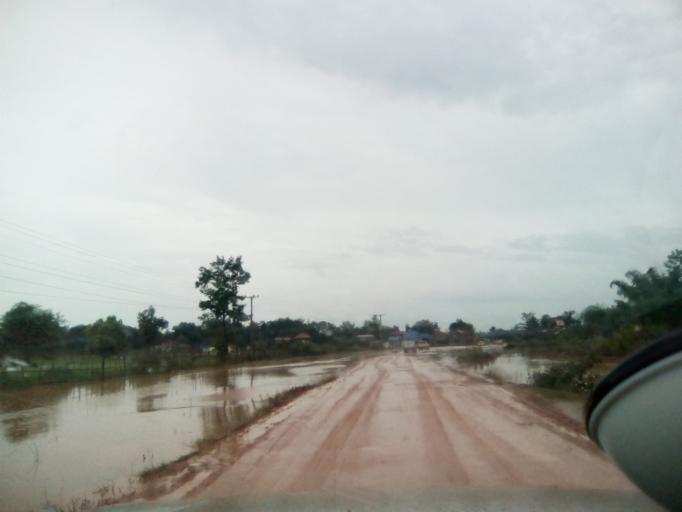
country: LA
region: Attapu
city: Attapu
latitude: 14.6990
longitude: 106.5314
